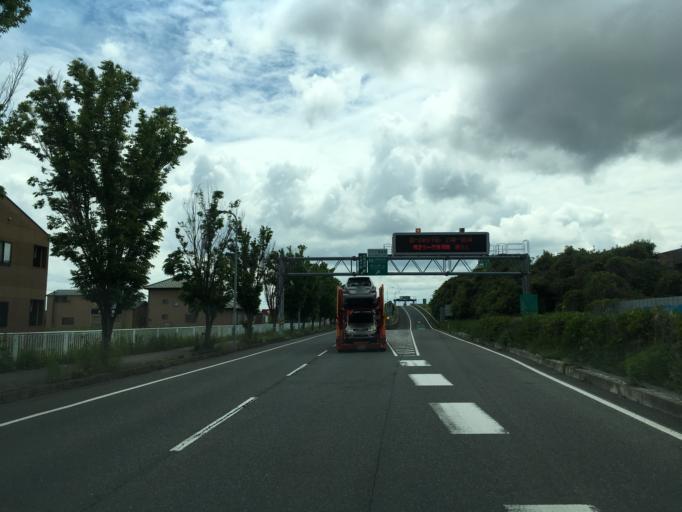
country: JP
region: Chiba
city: Kisarazu
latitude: 35.4312
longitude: 139.9256
